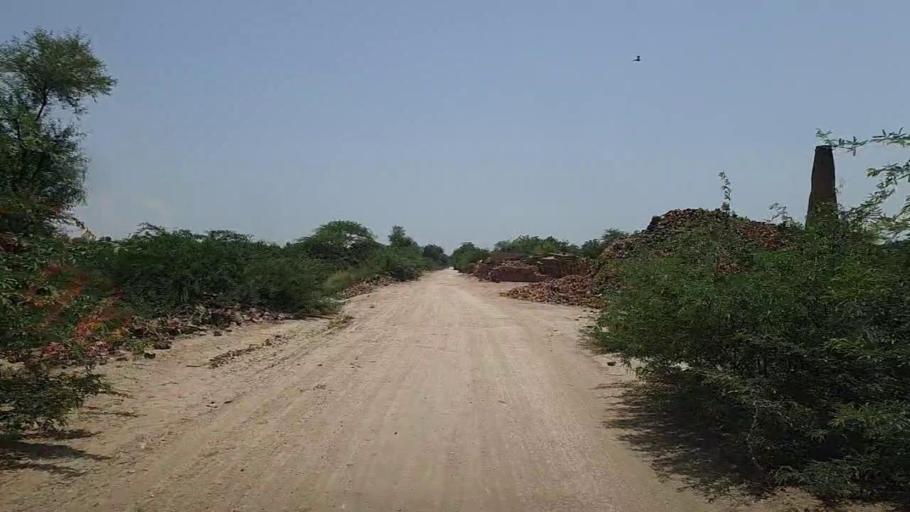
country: PK
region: Sindh
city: Pad Idan
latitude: 26.7606
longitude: 68.2936
